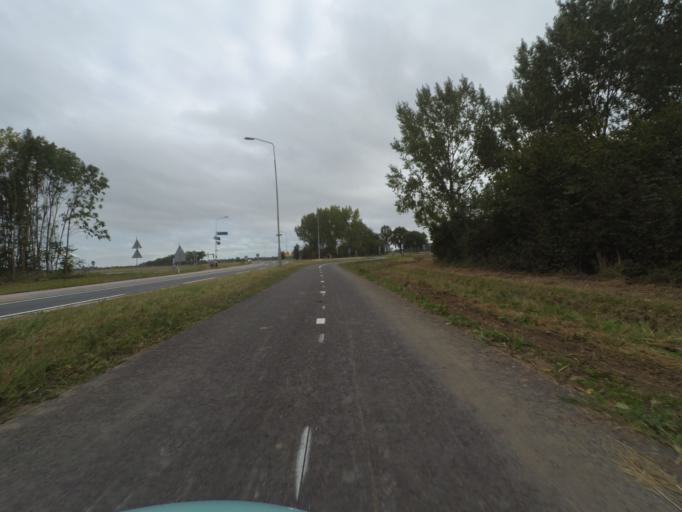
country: NL
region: Gelderland
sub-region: Gemeente Tiel
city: Tiel
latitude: 51.9363
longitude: 5.4490
